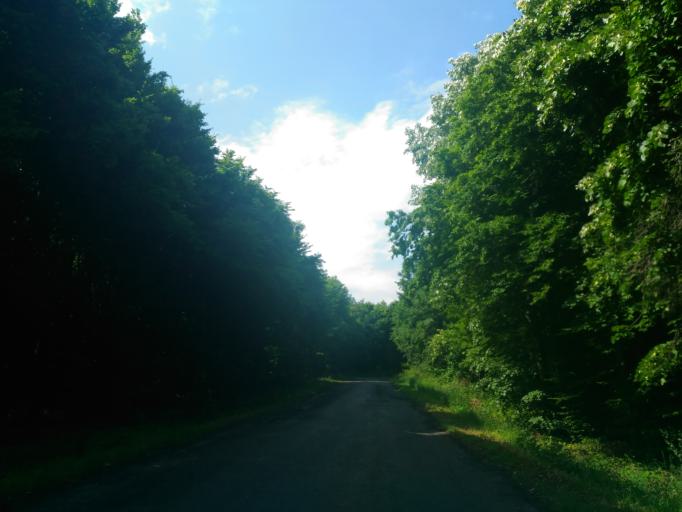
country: HU
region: Baranya
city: Pecs
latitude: 46.1318
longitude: 18.2320
